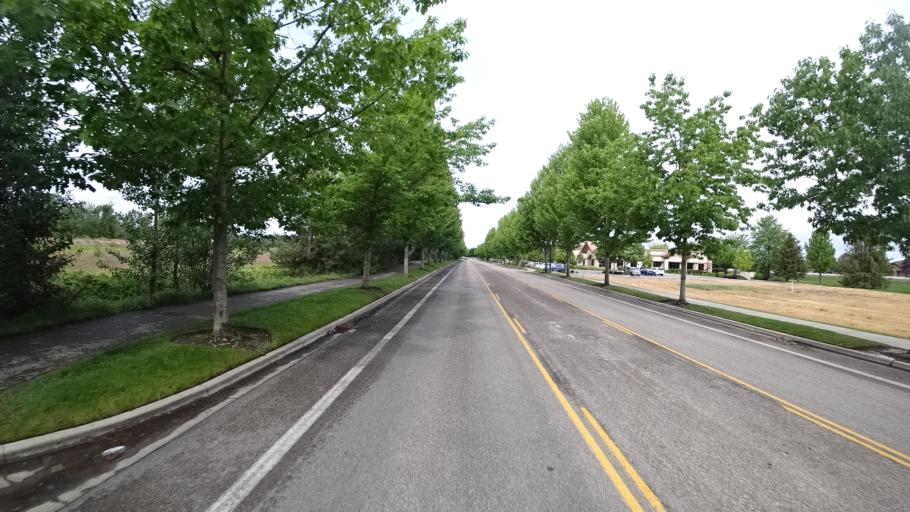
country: US
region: Idaho
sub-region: Ada County
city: Eagle
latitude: 43.6885
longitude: -116.3402
